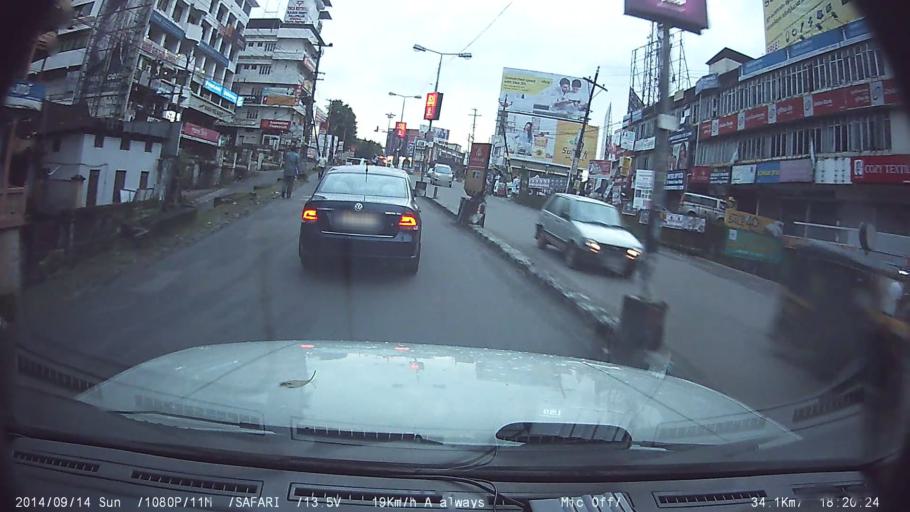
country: IN
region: Kerala
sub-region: Kottayam
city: Kottayam
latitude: 9.5918
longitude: 76.5233
